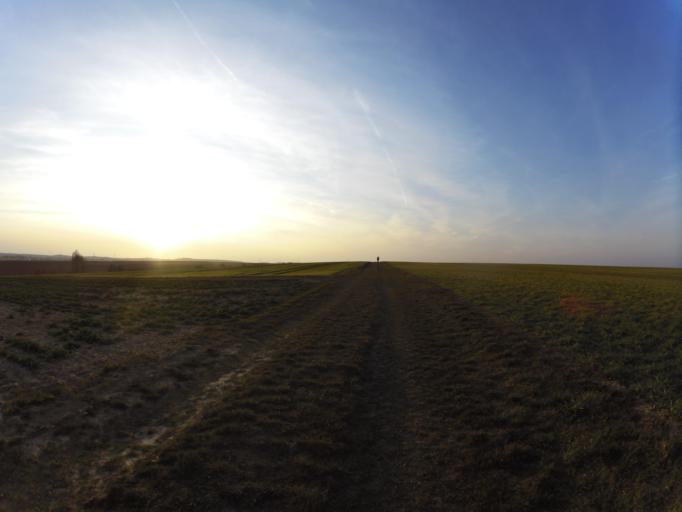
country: DE
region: Bavaria
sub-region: Regierungsbezirk Unterfranken
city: Prosselsheim
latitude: 49.8331
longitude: 10.1352
